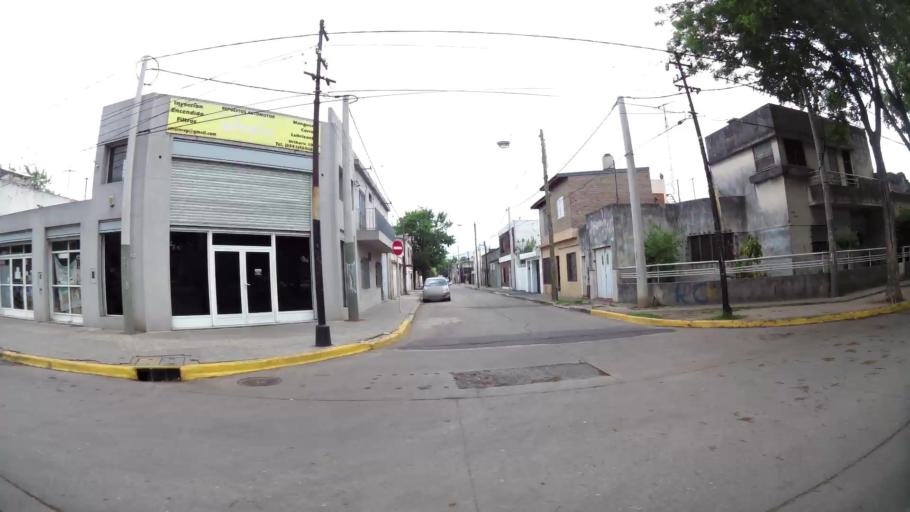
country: AR
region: Santa Fe
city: Gobernador Galvez
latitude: -32.9908
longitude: -60.6485
